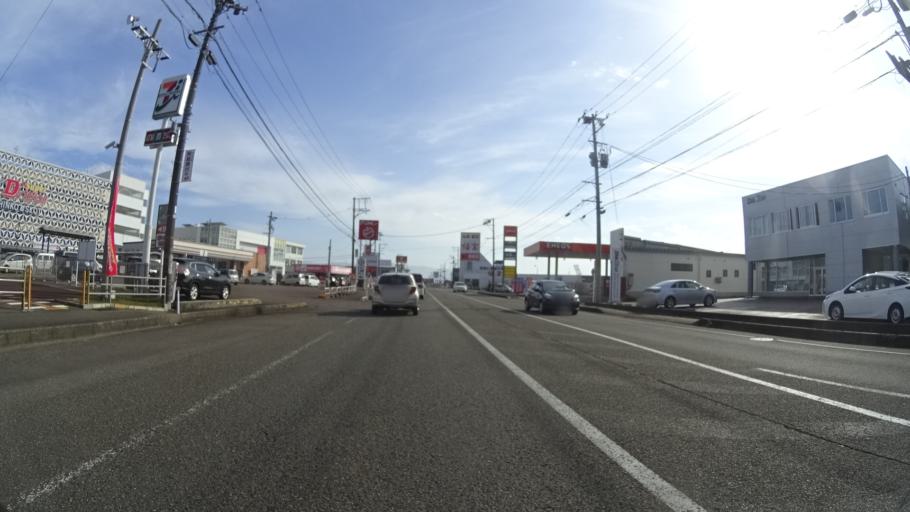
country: JP
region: Niigata
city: Joetsu
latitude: 37.1350
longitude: 138.2423
